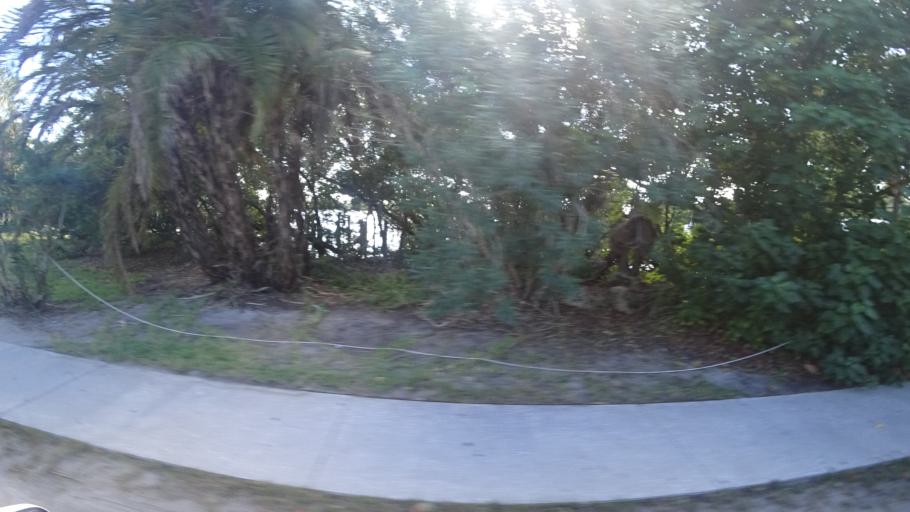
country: US
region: Florida
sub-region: Manatee County
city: Anna Maria
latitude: 27.5280
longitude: -82.7224
